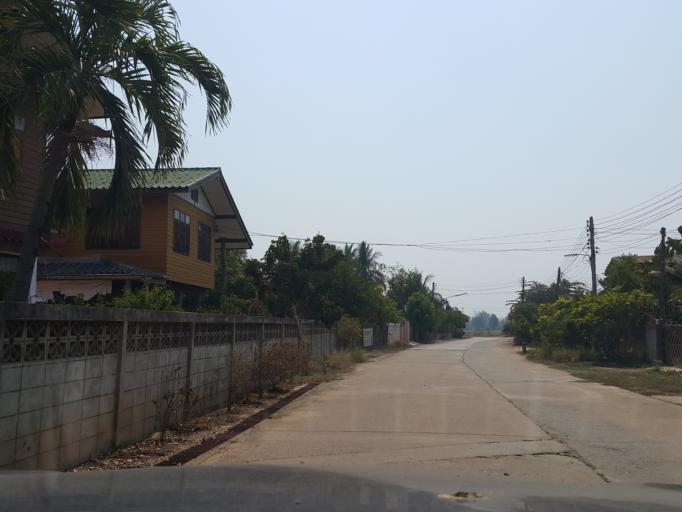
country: TH
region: Sukhothai
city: Thung Saliam
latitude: 17.3122
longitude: 99.5557
